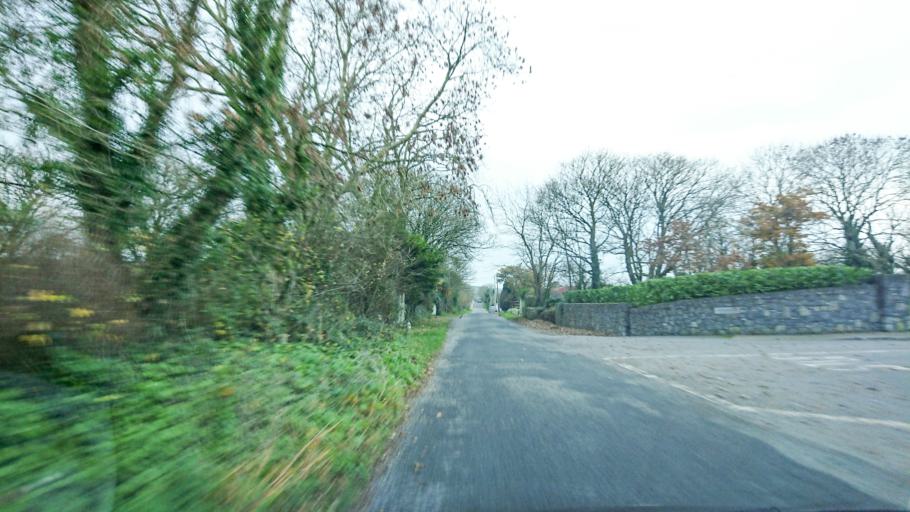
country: IE
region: Munster
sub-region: Waterford
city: Dunmore East
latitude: 52.2339
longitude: -6.9770
